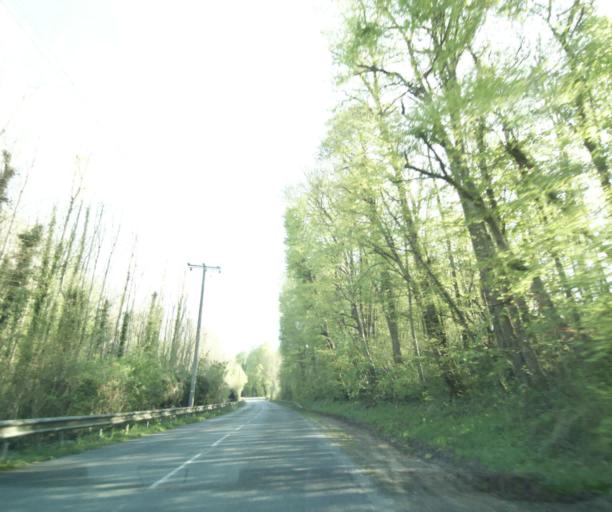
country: FR
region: Ile-de-France
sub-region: Departement de Seine-et-Marne
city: Vernou-la-Celle-sur-Seine
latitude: 48.4029
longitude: 2.8330
